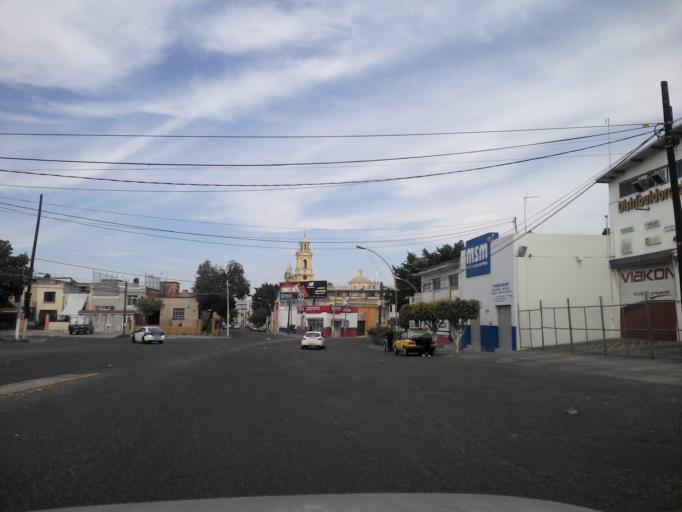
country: MX
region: Jalisco
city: Guadalajara
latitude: 20.6608
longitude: -103.3554
